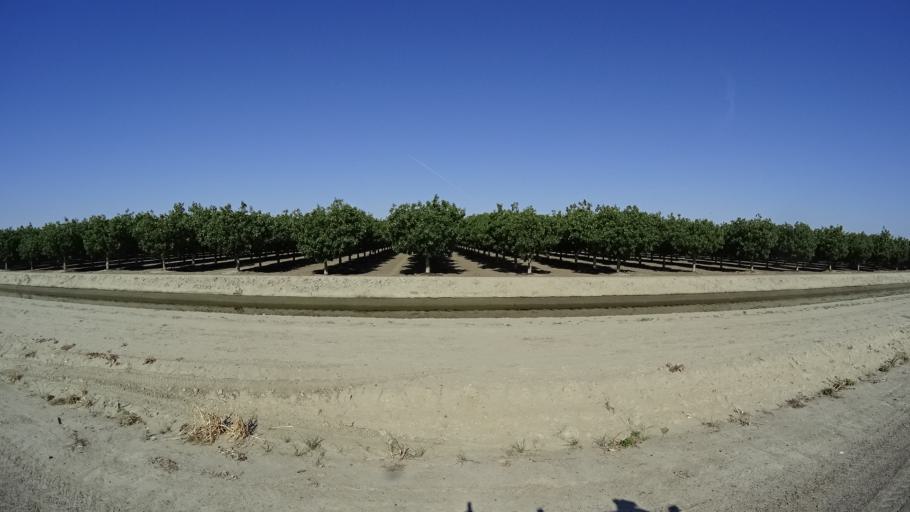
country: US
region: California
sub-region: Kings County
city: Corcoran
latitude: 36.0856
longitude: -119.5899
